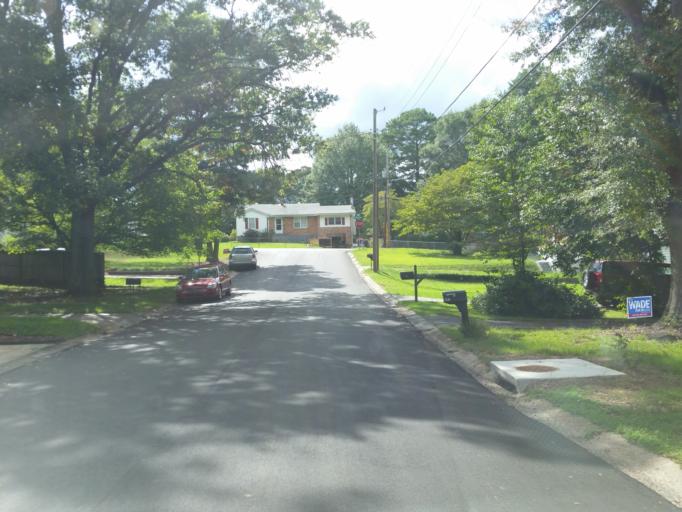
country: US
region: Georgia
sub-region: Cobb County
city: Smyrna
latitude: 33.8771
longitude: -84.5260
